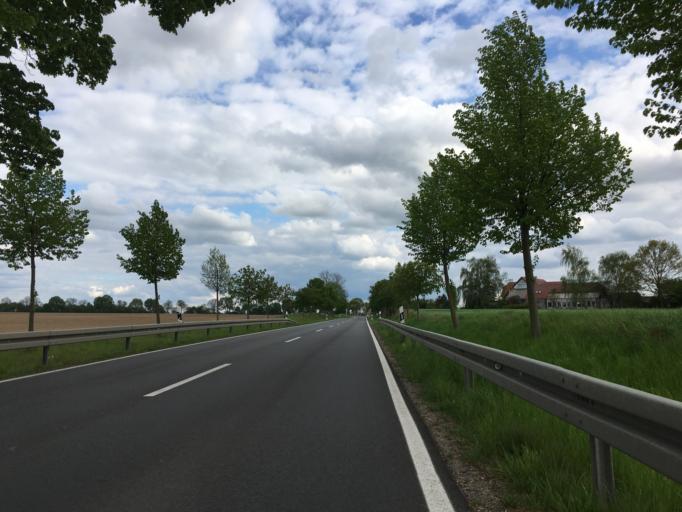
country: DE
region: Brandenburg
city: Bernau bei Berlin
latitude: 52.6591
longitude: 13.5989
